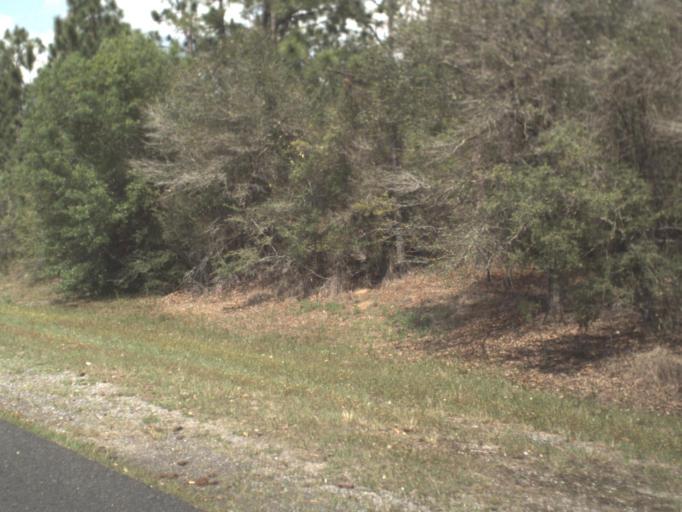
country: US
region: Florida
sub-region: Escambia County
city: Molino
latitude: 30.8095
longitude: -87.3356
